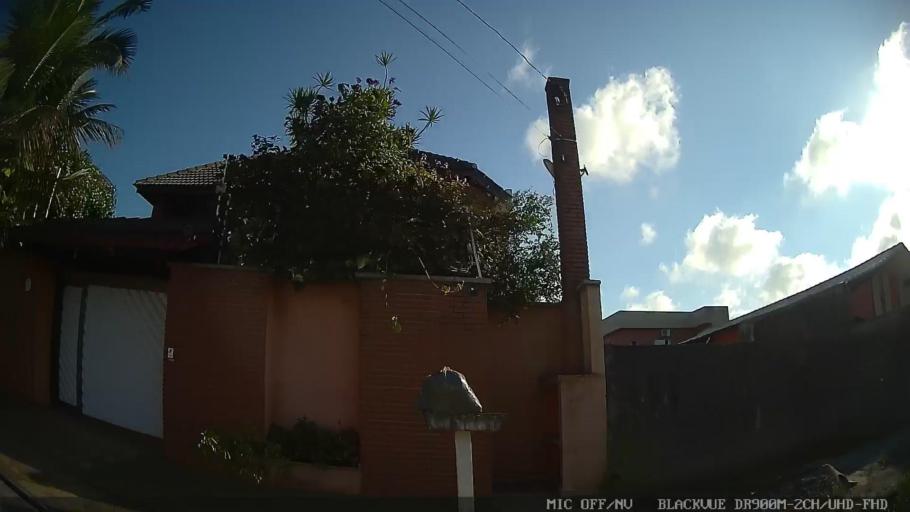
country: BR
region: Sao Paulo
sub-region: Peruibe
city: Peruibe
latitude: -24.2873
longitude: -46.9643
